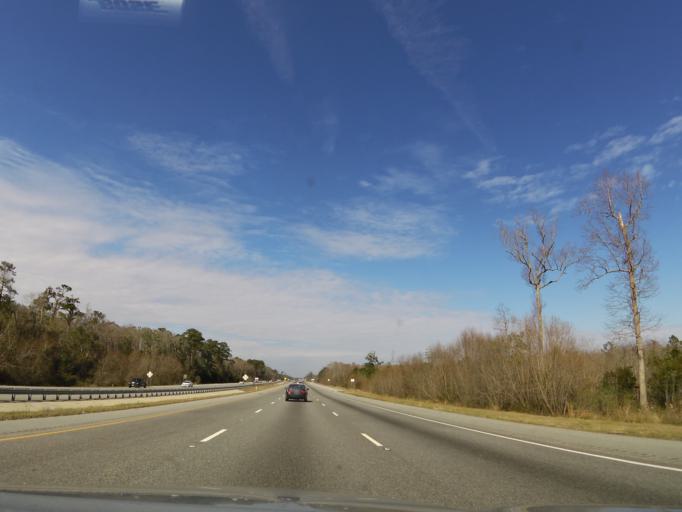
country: US
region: Georgia
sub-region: McIntosh County
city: Darien
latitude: 31.4366
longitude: -81.4440
